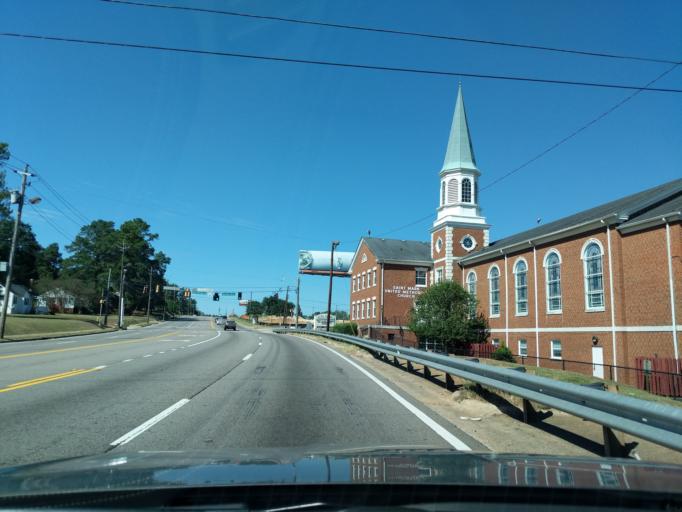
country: US
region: Georgia
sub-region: Richmond County
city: Augusta
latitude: 33.4990
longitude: -82.0116
